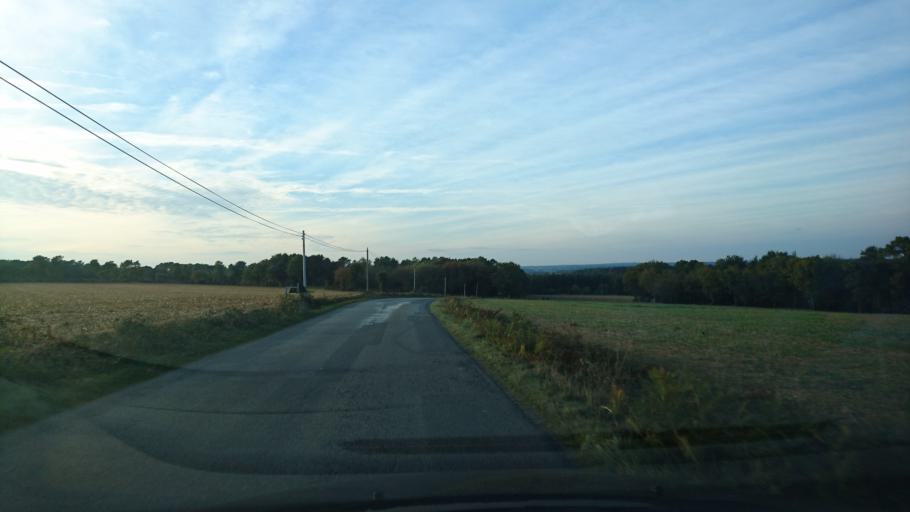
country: FR
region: Brittany
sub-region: Departement d'Ille-et-Vilaine
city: Sixt-sur-Aff
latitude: 47.7633
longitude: -2.0684
